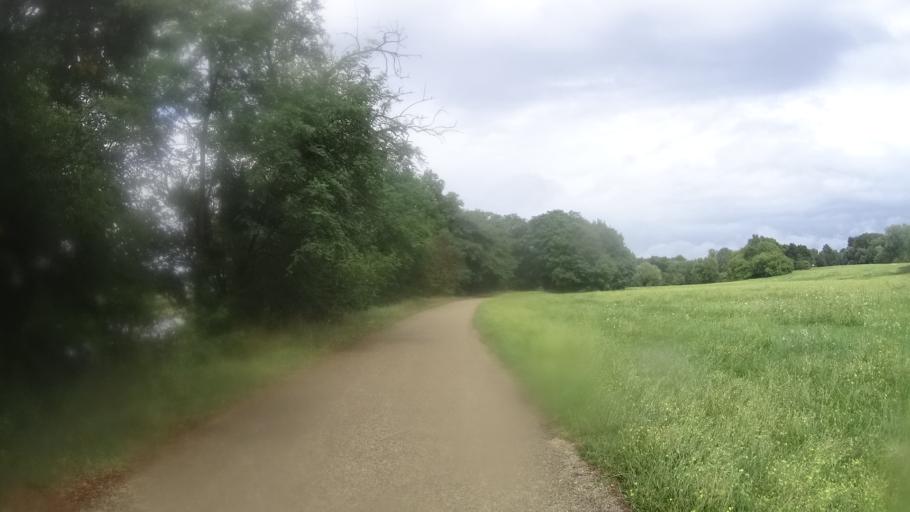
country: FR
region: Centre
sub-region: Departement du Loiret
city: Saint-Jean-le-Blanc
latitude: 47.8968
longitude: 1.9292
